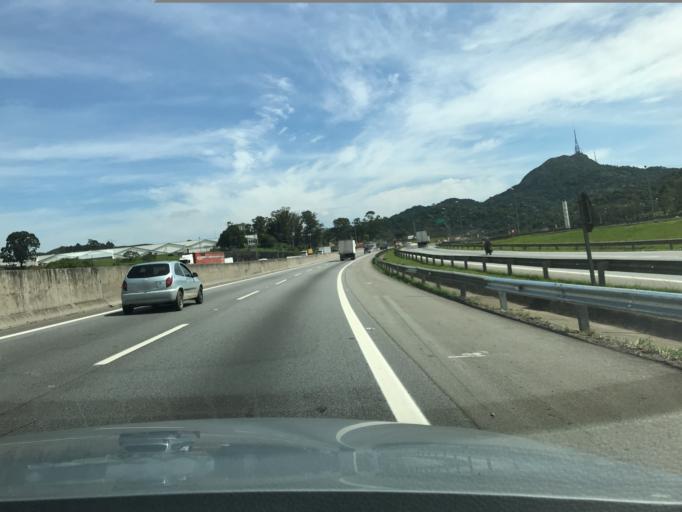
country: BR
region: Sao Paulo
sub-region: Osasco
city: Osasco
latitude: -23.4837
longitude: -46.7702
